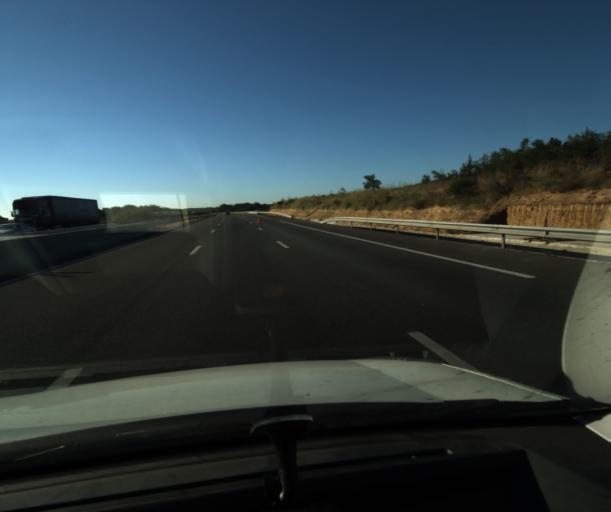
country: FR
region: Midi-Pyrenees
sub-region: Departement du Tarn-et-Garonne
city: Pompignan
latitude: 43.8235
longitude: 1.3464
